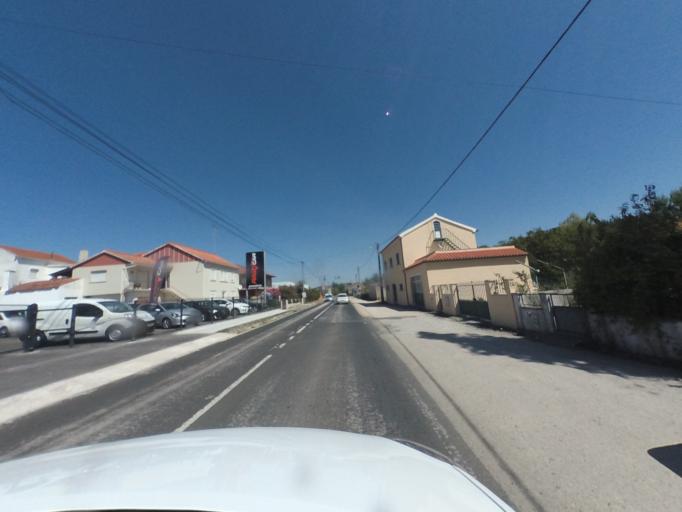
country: PT
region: Leiria
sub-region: Alcobaca
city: Alcobaca
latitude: 39.5205
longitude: -9.0099
